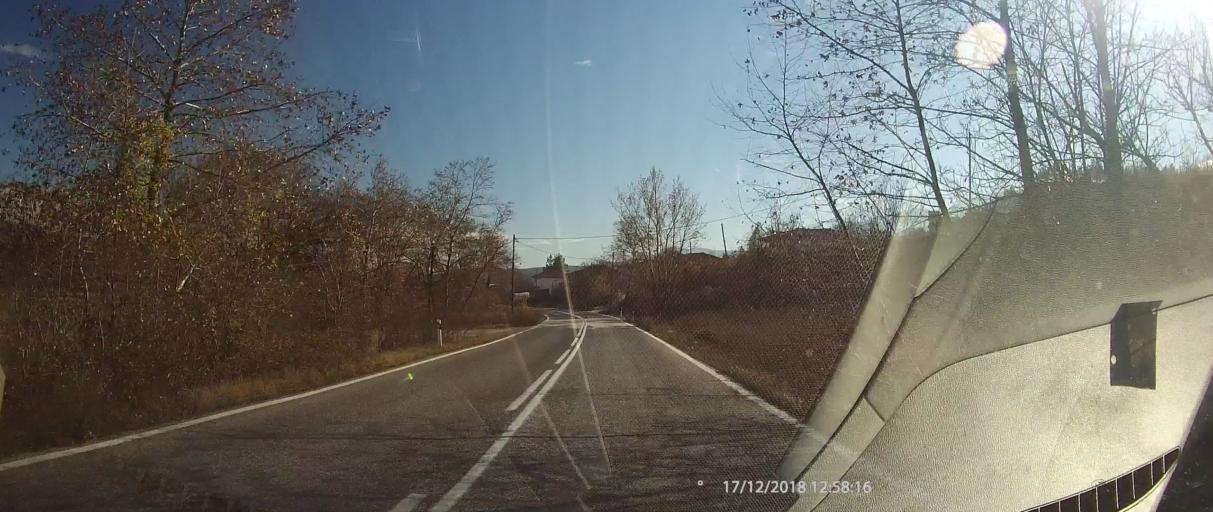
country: GR
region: Thessaly
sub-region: Trikala
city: Kastraki
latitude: 39.7405
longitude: 21.5399
